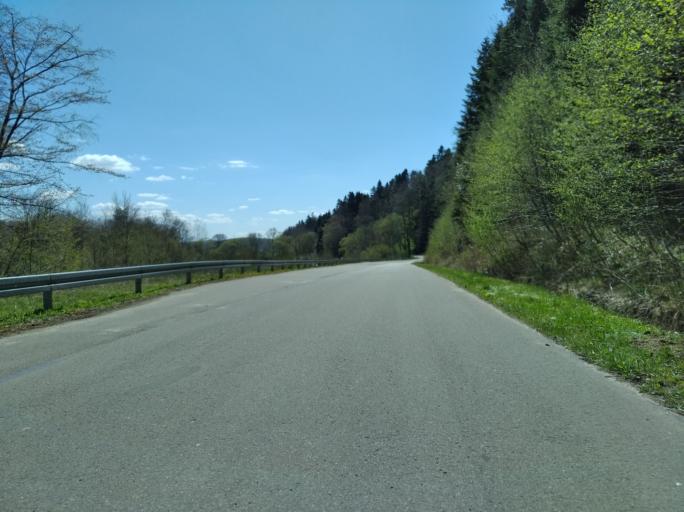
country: PL
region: Subcarpathian Voivodeship
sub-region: Powiat brzozowski
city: Dydnia
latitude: 49.6865
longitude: 22.2378
